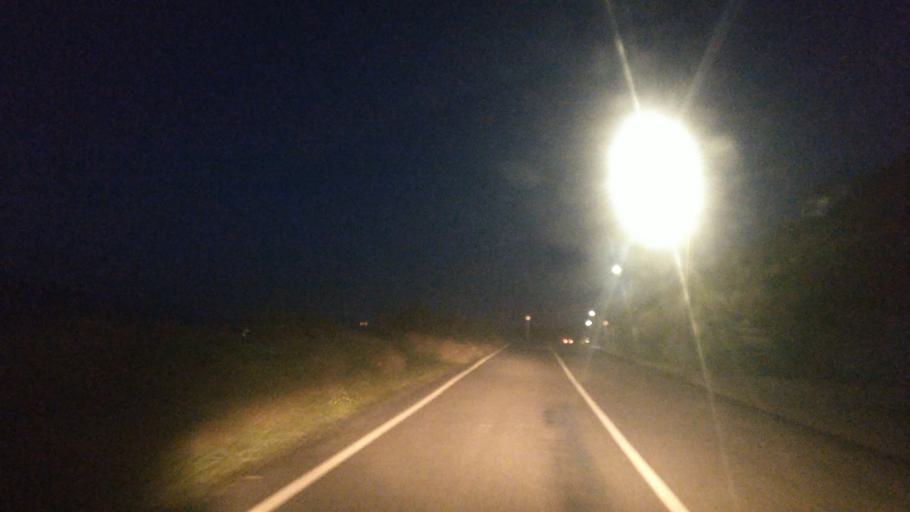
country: NZ
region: Wellington
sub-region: Kapiti Coast District
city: Paraparaumu
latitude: -40.9781
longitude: 174.9564
